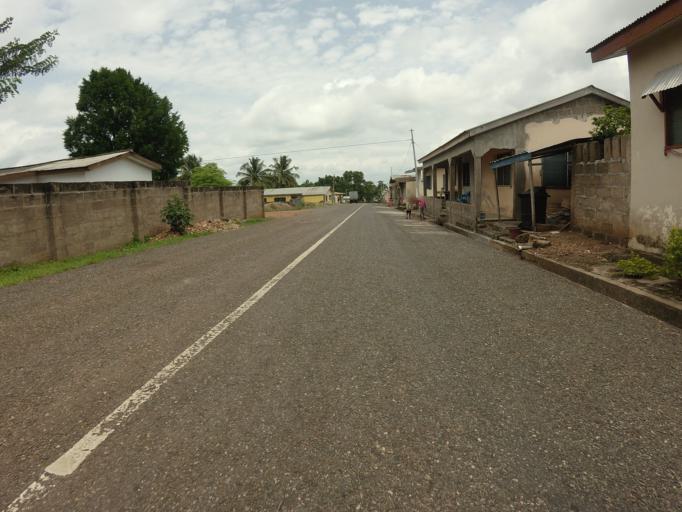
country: GH
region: Volta
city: Ho
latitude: 6.5924
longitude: 0.4772
